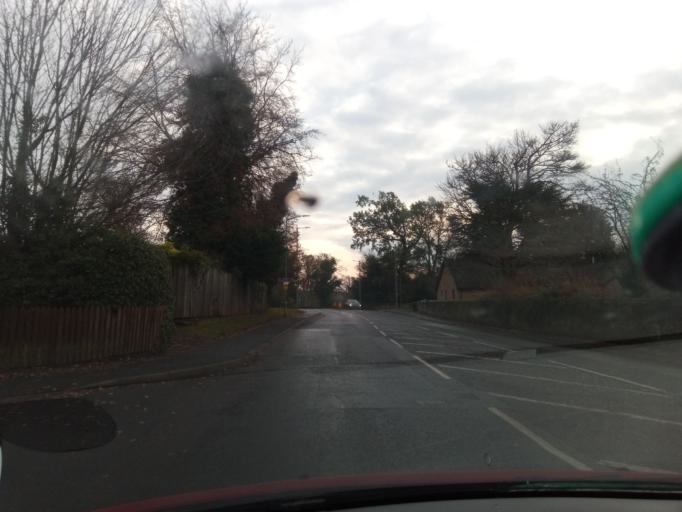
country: GB
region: Scotland
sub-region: The Scottish Borders
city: Kelso
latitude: 55.6040
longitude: -2.4289
